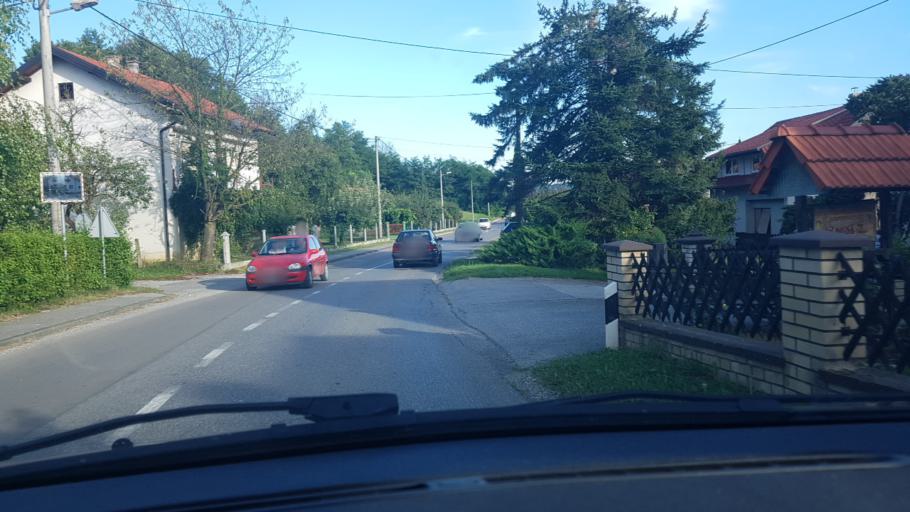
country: HR
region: Krapinsko-Zagorska
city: Bedekovcina
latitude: 46.0440
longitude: 15.9796
